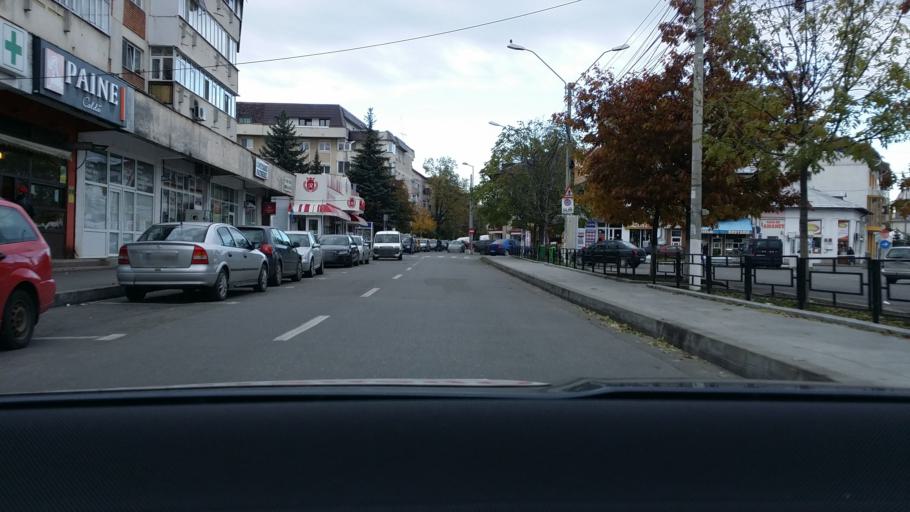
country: RO
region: Prahova
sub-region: Municipiul Campina
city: Campina
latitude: 45.1242
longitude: 25.7361
